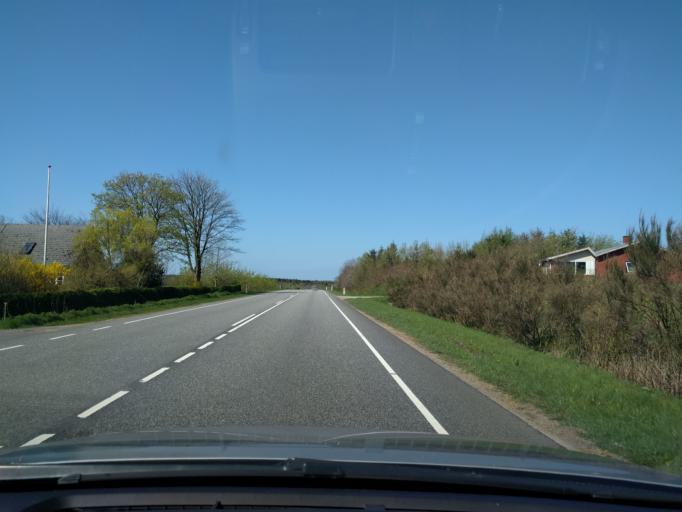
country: DK
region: Central Jutland
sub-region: Ringkobing-Skjern Kommune
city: Skjern
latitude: 56.0843
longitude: 8.4775
